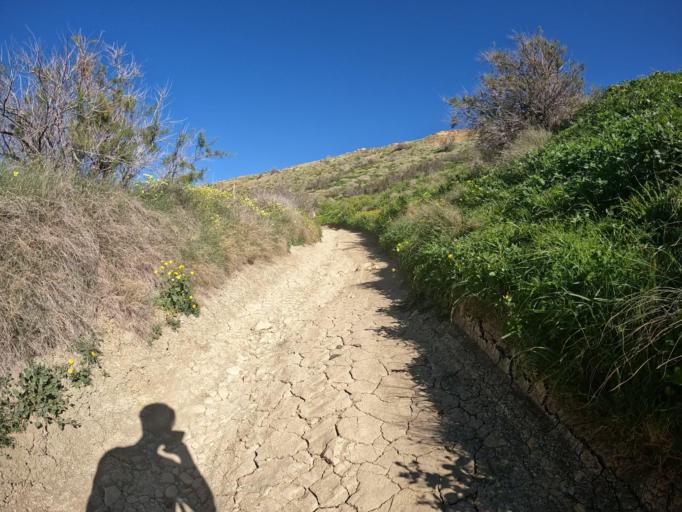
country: MT
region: L-Imgarr
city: Imgarr
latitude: 35.9293
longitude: 14.3460
